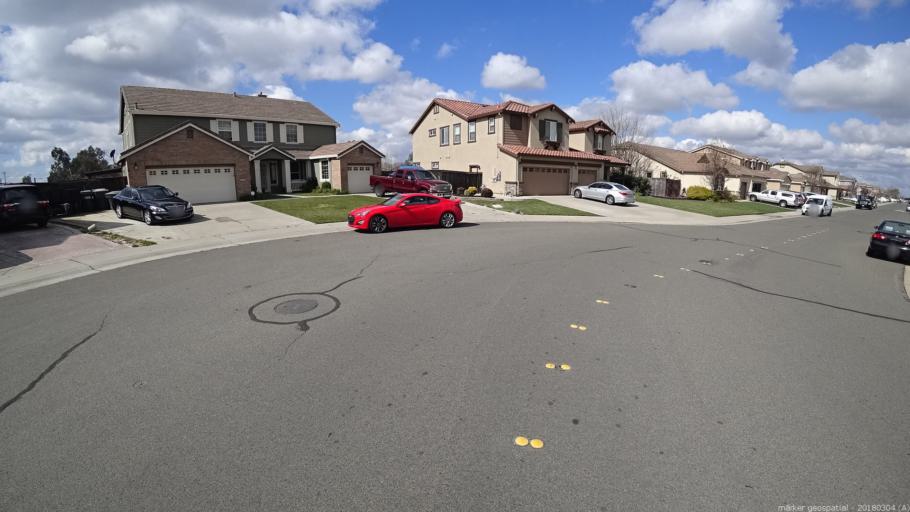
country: US
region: California
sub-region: Sacramento County
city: Vineyard
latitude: 38.4540
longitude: -121.3268
